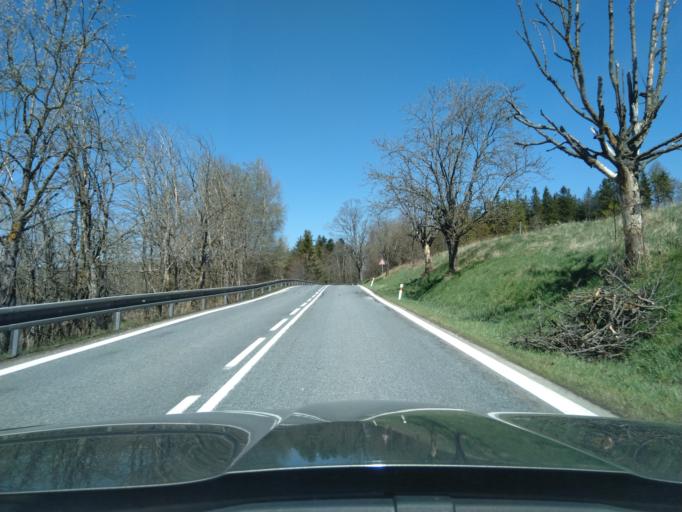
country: CZ
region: Jihocesky
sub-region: Okres Prachatice
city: Vimperk
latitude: 49.0341
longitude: 13.7622
